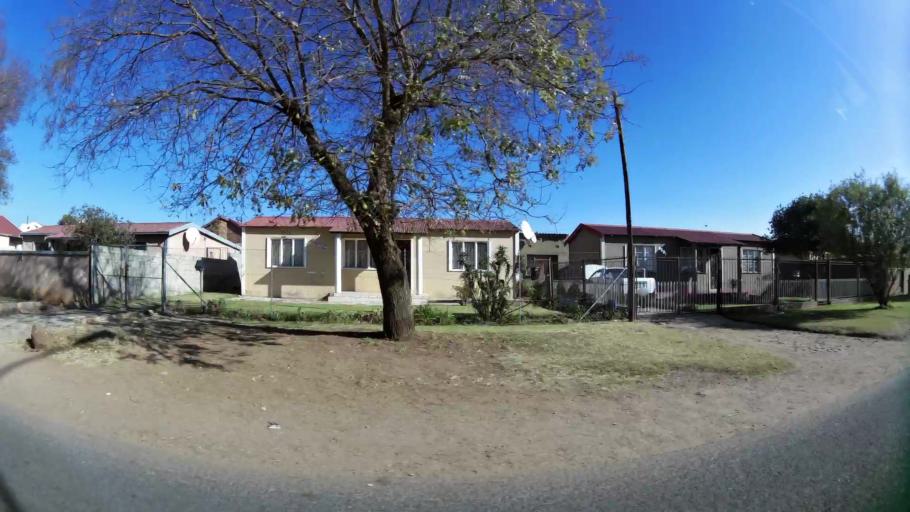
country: ZA
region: Gauteng
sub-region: City of Johannesburg Metropolitan Municipality
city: Roodepoort
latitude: -26.2217
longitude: 27.9180
